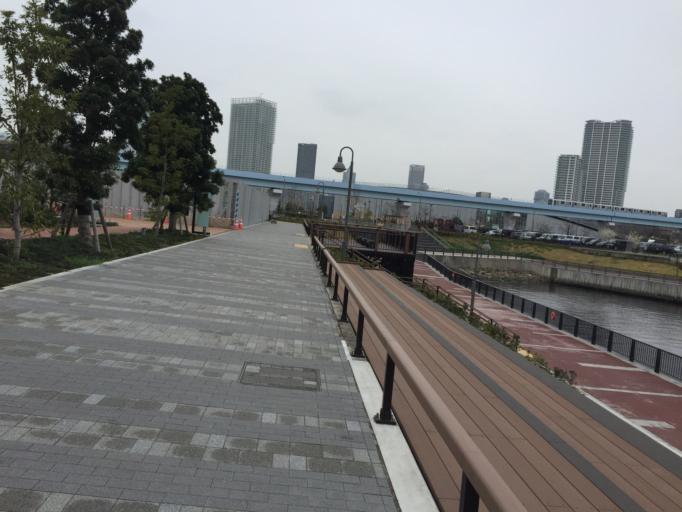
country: JP
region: Tokyo
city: Urayasu
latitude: 35.6497
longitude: 139.7935
